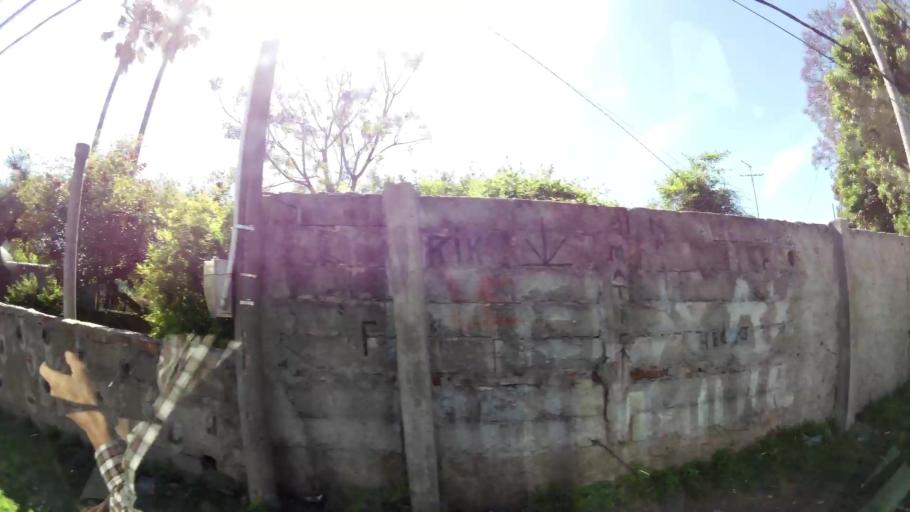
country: UY
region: Montevideo
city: Montevideo
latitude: -34.8680
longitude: -56.1285
